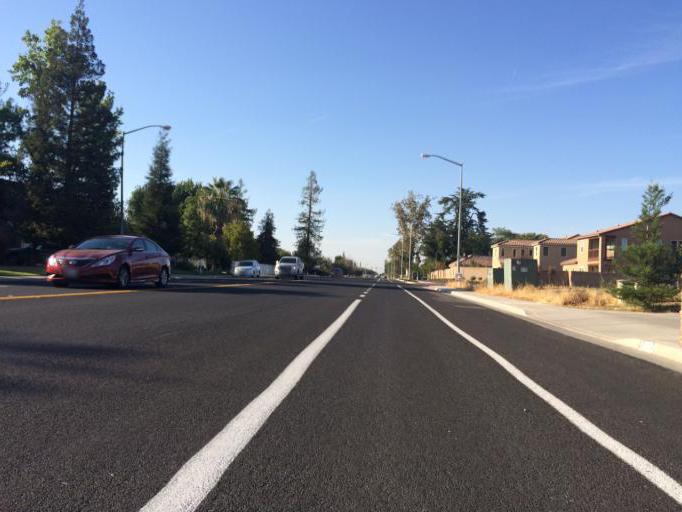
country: US
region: California
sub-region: Fresno County
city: Tarpey Village
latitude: 36.7957
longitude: -119.6730
